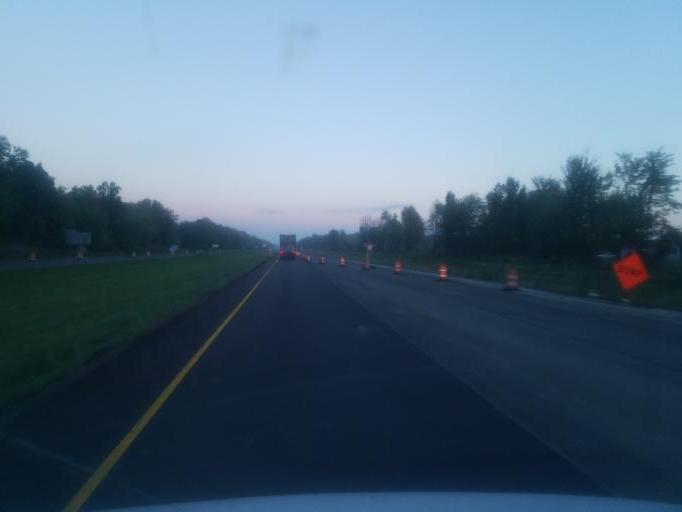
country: US
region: Ohio
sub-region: Ashtabula County
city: Jefferson
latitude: 41.7550
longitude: -80.7139
